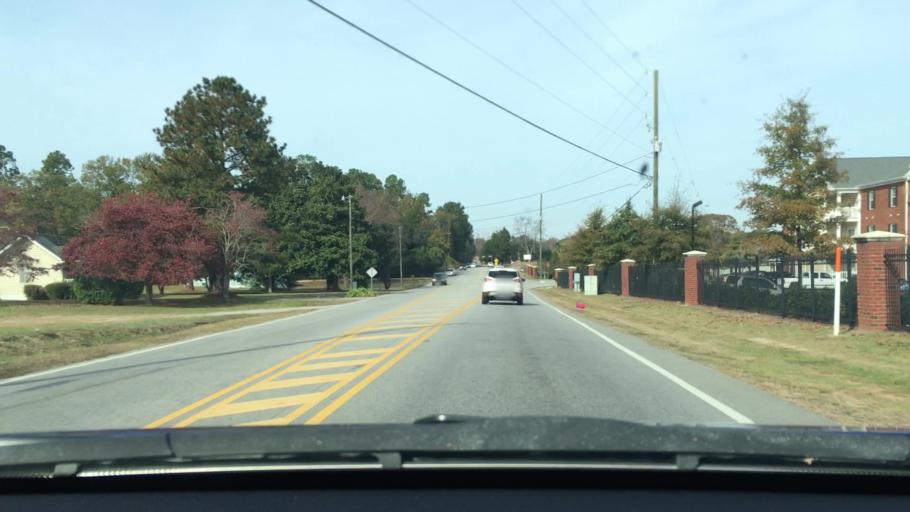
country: US
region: South Carolina
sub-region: Sumter County
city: South Sumter
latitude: 33.9014
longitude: -80.3702
